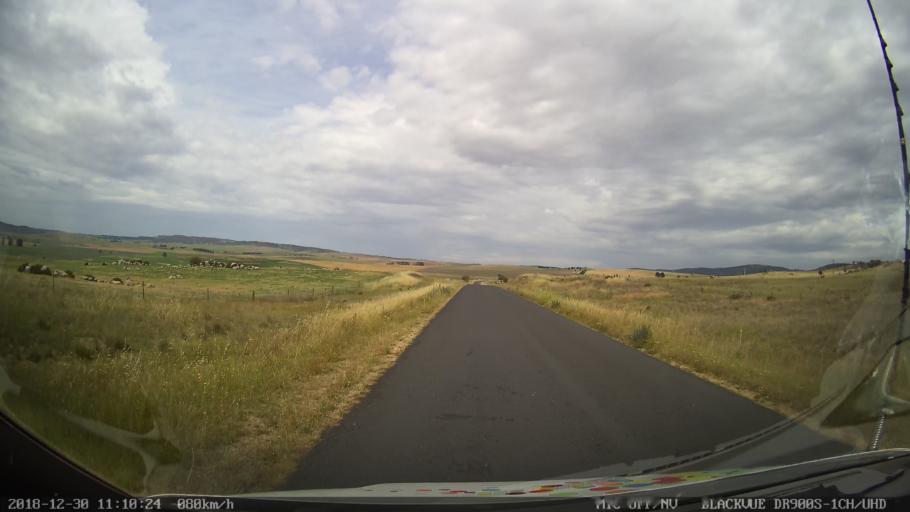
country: AU
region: New South Wales
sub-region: Snowy River
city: Berridale
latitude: -36.5144
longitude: 148.7819
